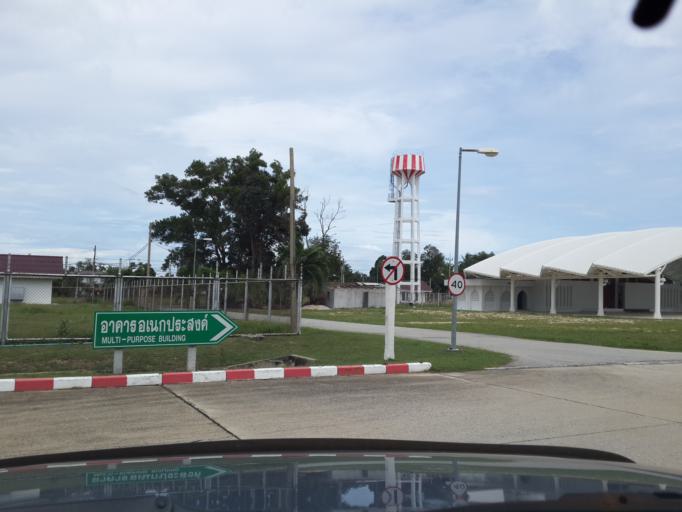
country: TH
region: Narathiwat
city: Bacho
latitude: 6.5235
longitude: 101.7495
